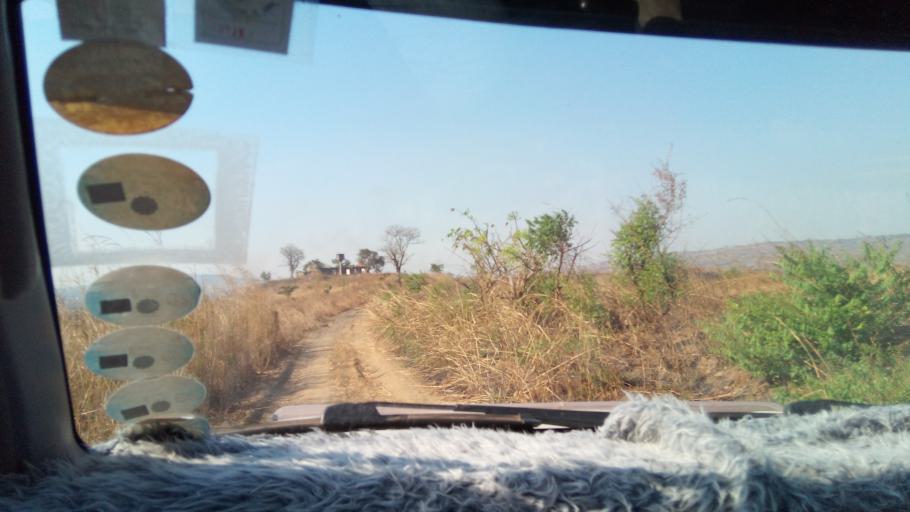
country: CD
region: Katanga
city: Kalemie
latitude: -5.9093
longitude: 29.1244
